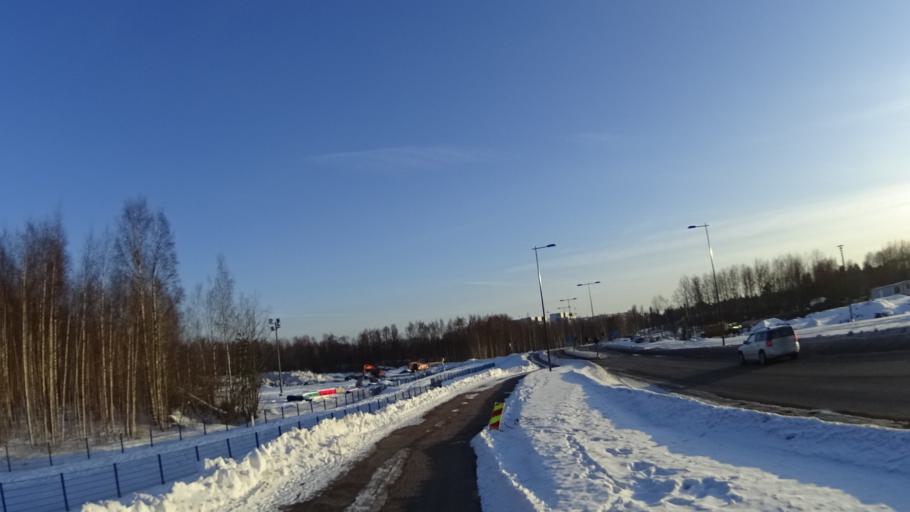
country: FI
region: Uusimaa
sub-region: Helsinki
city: Teekkarikylae
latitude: 60.2145
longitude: 24.8357
